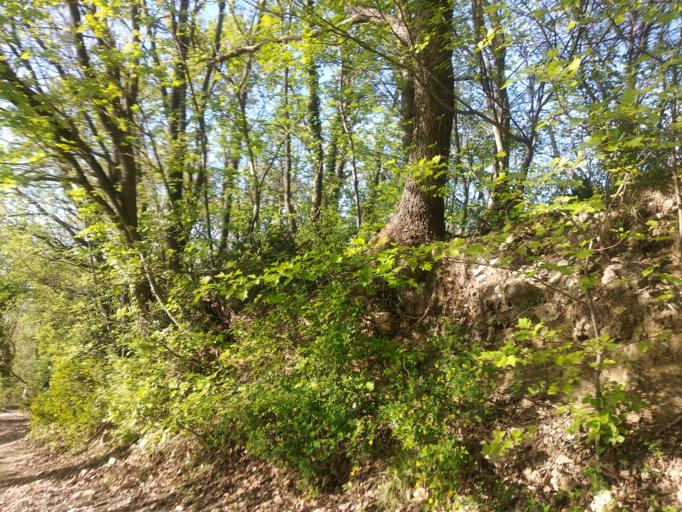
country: IT
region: Emilia-Romagna
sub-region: Provincia di Ravenna
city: Fognano
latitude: 44.2240
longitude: 11.7393
